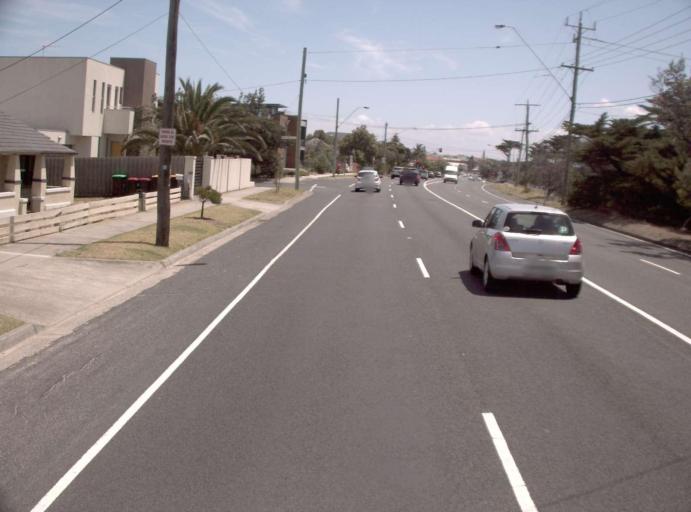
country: AU
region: Victoria
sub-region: Kingston
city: Mordialloc
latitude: -38.0139
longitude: 145.0915
